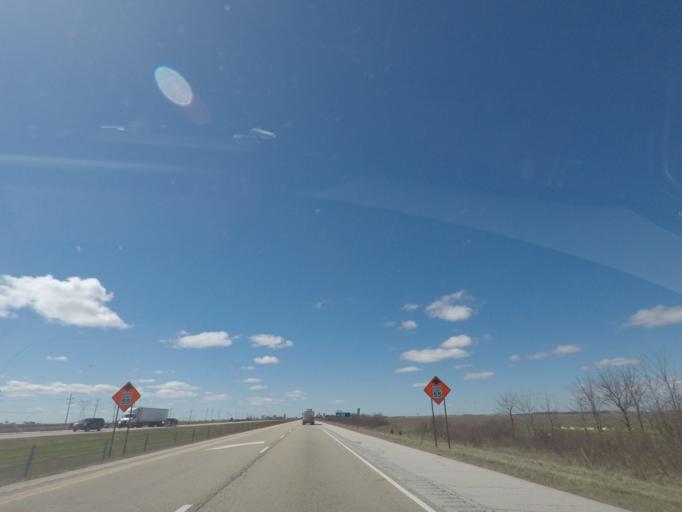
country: US
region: Illinois
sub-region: Livingston County
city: Dwight
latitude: 41.1312
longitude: -88.3809
